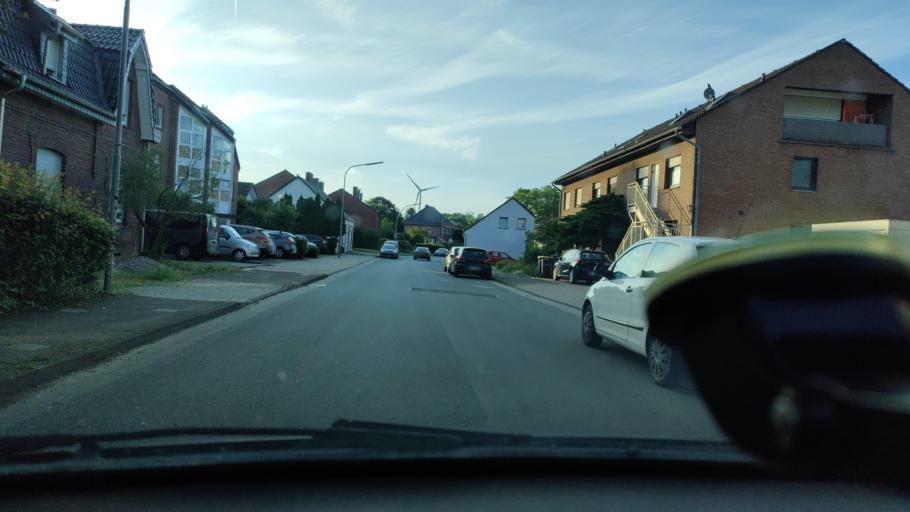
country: DE
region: North Rhine-Westphalia
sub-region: Regierungsbezirk Dusseldorf
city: Rheurdt
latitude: 51.4704
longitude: 6.4679
